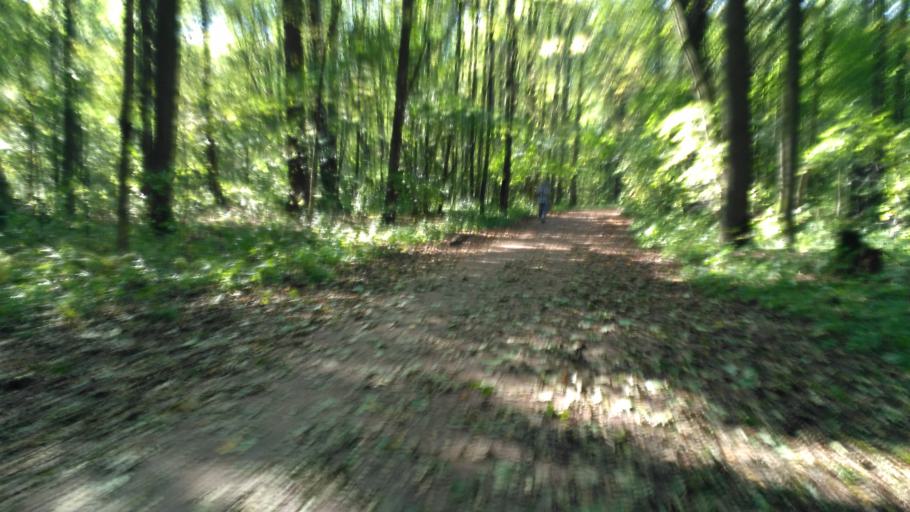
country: RU
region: Moskovskaya
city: Izmaylovo
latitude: 55.7826
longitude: 37.7752
